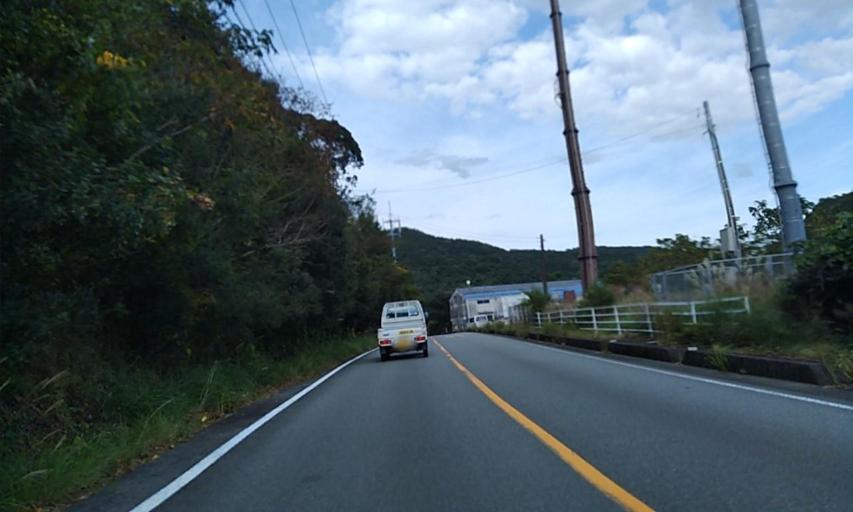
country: JP
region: Mie
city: Ise
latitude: 34.3096
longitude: 136.6365
